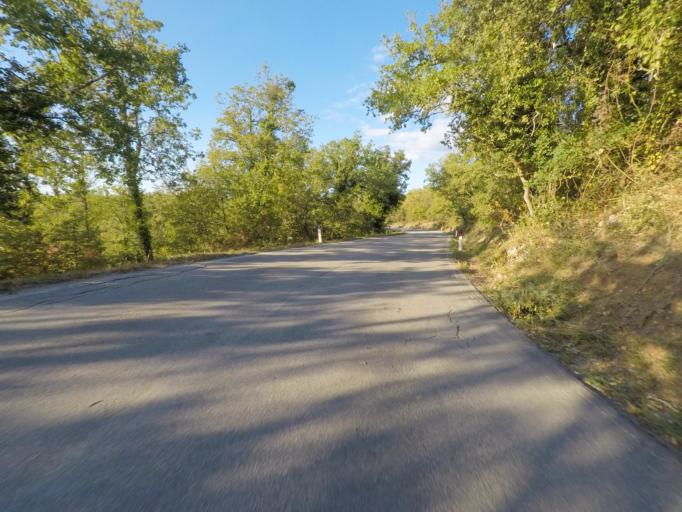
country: IT
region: Tuscany
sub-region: Provincia di Siena
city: Radda in Chianti
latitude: 43.4526
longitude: 11.3860
